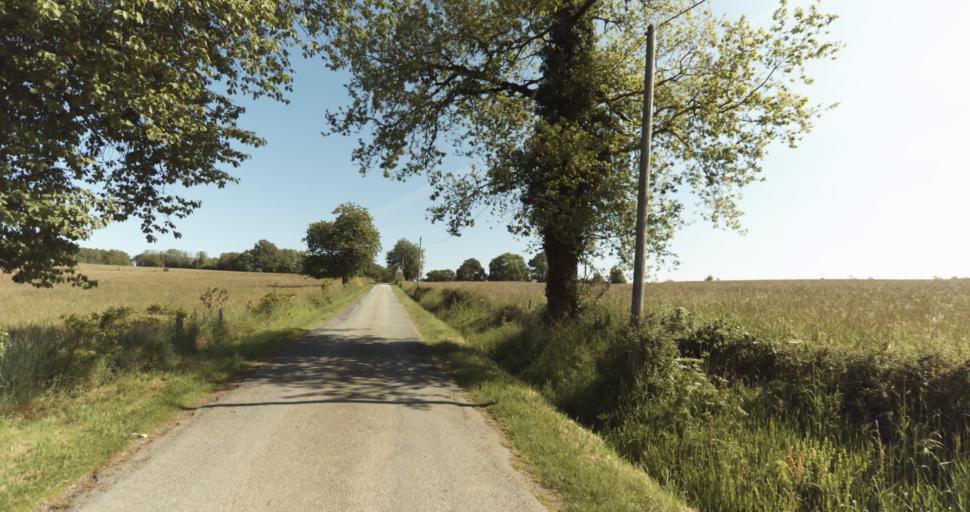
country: FR
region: Limousin
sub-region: Departement de la Haute-Vienne
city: Solignac
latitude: 45.7139
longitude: 1.2655
